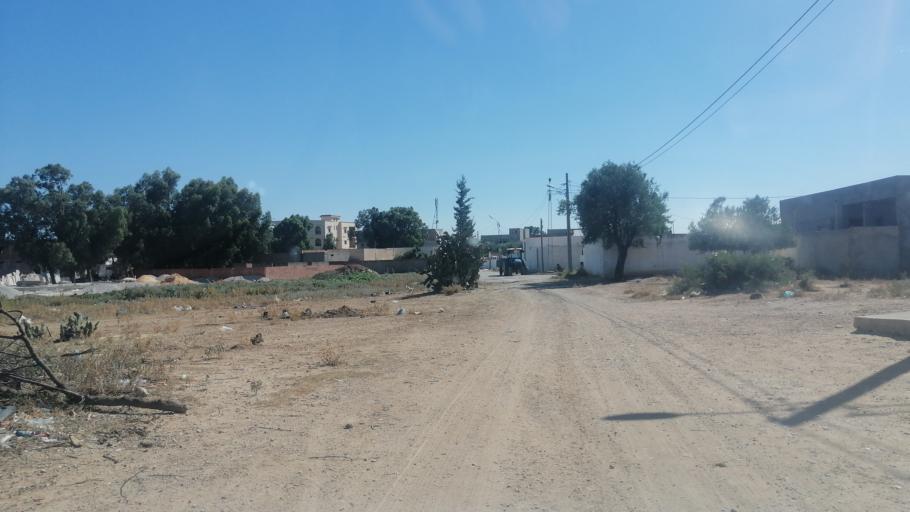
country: TN
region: Al Qayrawan
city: Sbikha
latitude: 36.1270
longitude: 10.0971
